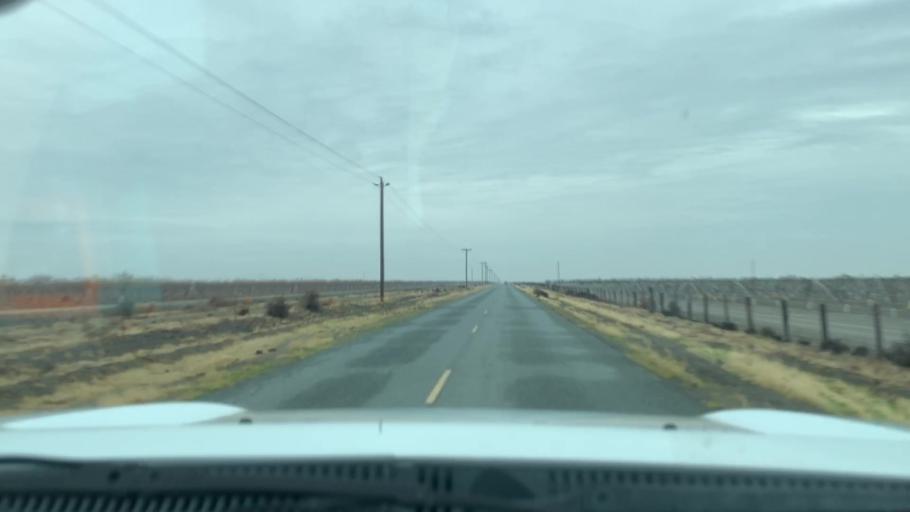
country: US
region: California
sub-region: Tulare County
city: Alpaugh
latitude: 35.7608
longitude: -119.5682
